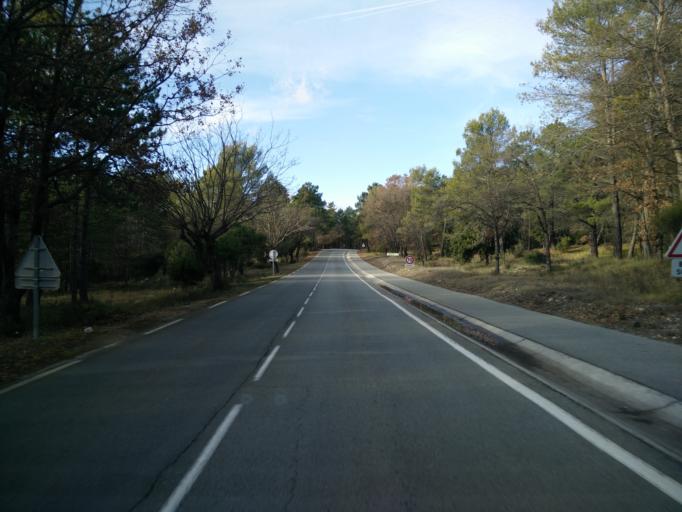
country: FR
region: Provence-Alpes-Cote d'Azur
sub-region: Departement des Alpes-Maritimes
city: Le Tignet
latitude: 43.6443
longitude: 6.8270
